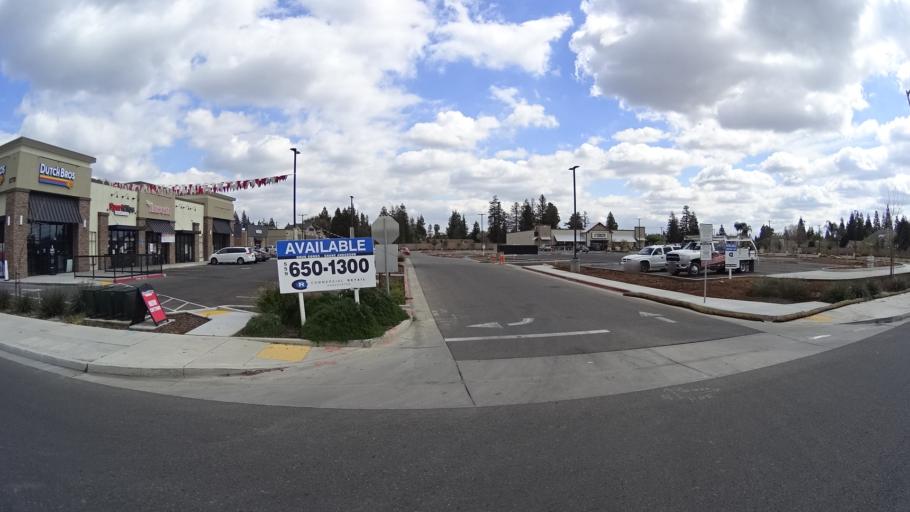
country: US
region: California
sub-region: Fresno County
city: Fresno
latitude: 36.8365
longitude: -119.8624
